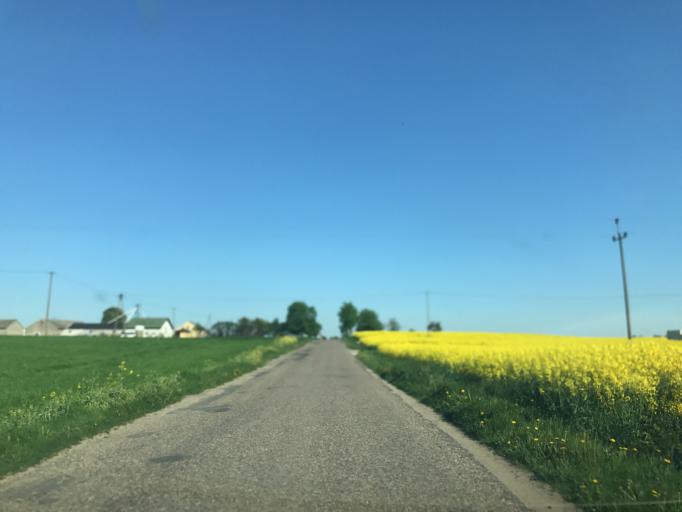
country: PL
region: Kujawsko-Pomorskie
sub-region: Powiat brodnicki
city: Bartniczka
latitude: 53.2068
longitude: 19.5875
